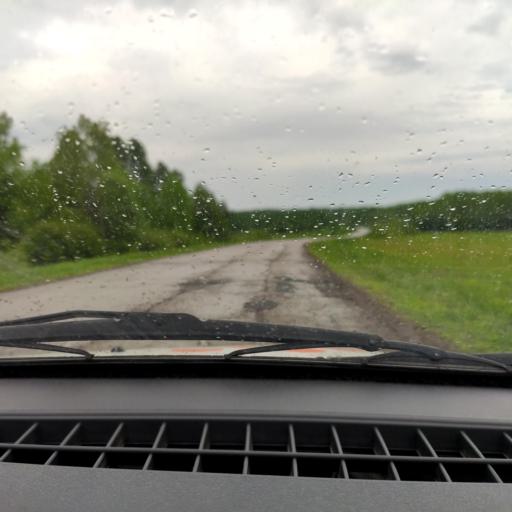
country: RU
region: Bashkortostan
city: Kudeyevskiy
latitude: 54.8512
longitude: 56.8110
